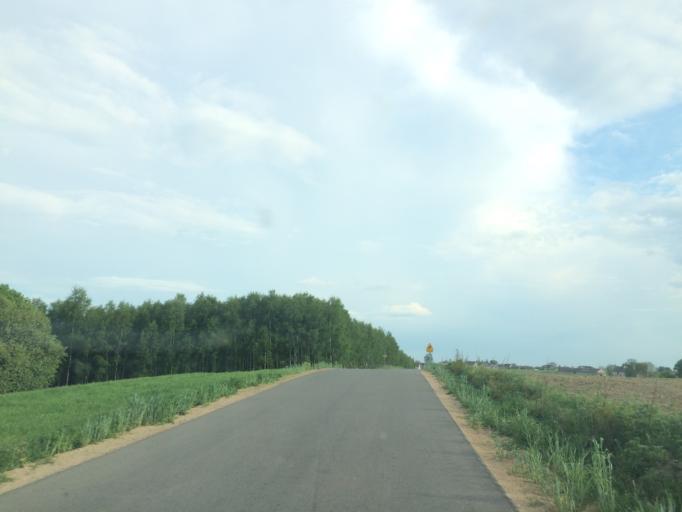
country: PL
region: Kujawsko-Pomorskie
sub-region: Powiat brodnicki
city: Brzozie
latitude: 53.3663
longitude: 19.7101
